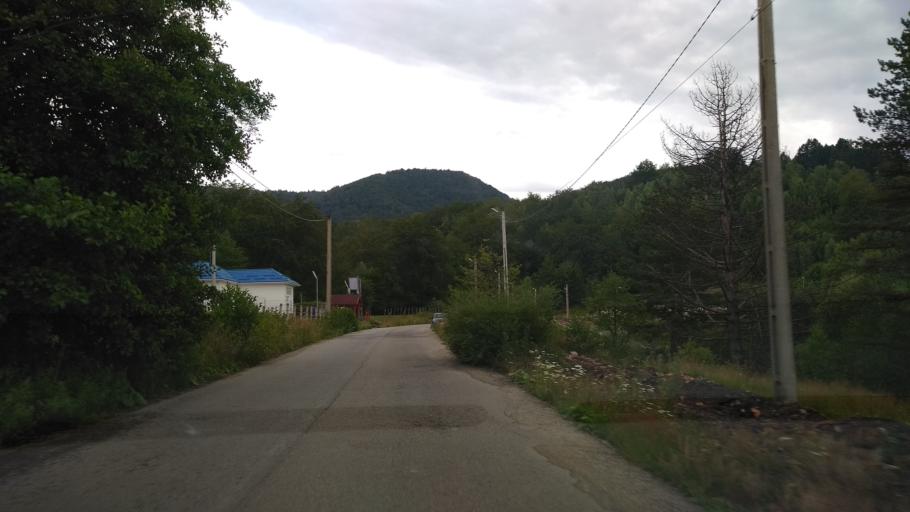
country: RO
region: Hunedoara
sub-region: Municipiul  Vulcan
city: Jiu-Paroseni
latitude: 45.3557
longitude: 23.2899
